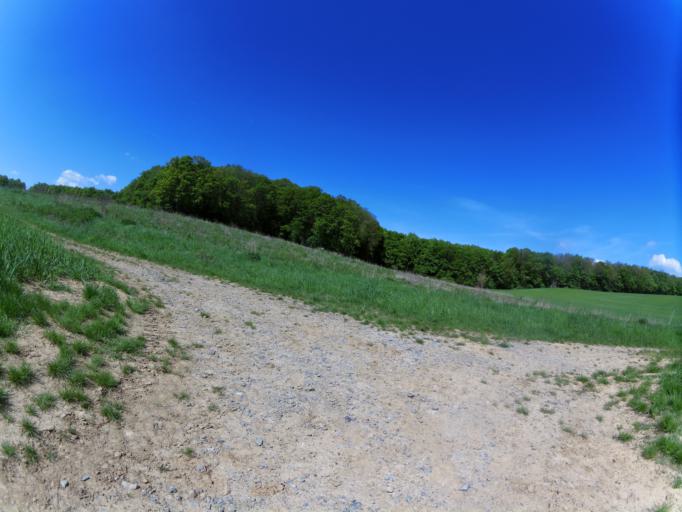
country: DE
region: Bavaria
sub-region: Regierungsbezirk Unterfranken
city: Rimpar
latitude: 49.8790
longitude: 9.9975
